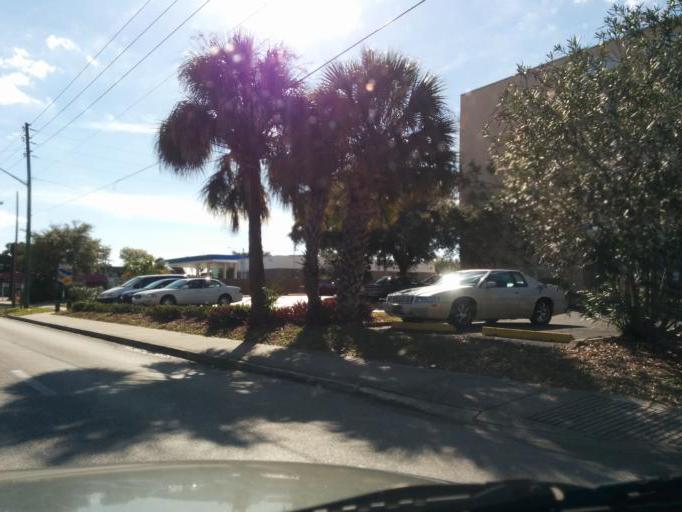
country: US
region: Florida
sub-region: Pinellas County
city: Lealman
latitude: 27.8094
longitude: -82.6345
